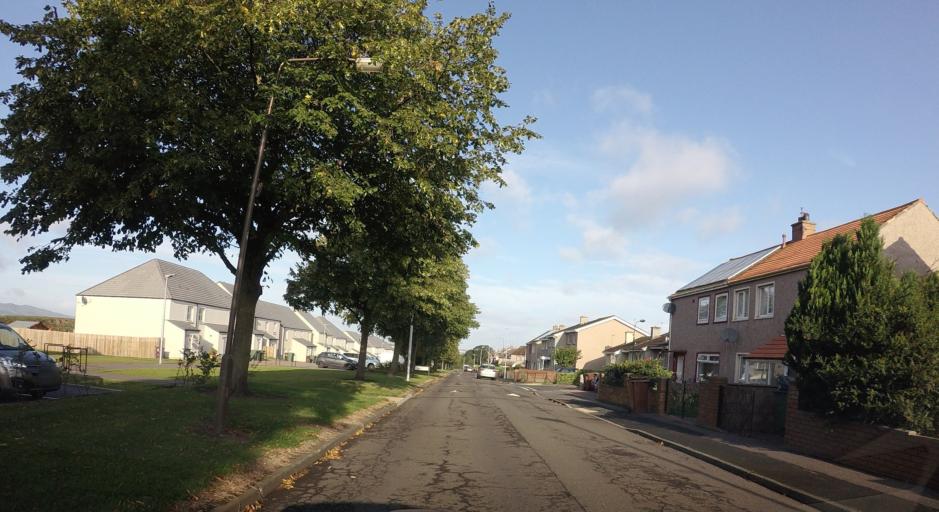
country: GB
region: Scotland
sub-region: East Lothian
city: Musselburgh
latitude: 55.9333
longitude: -3.0144
